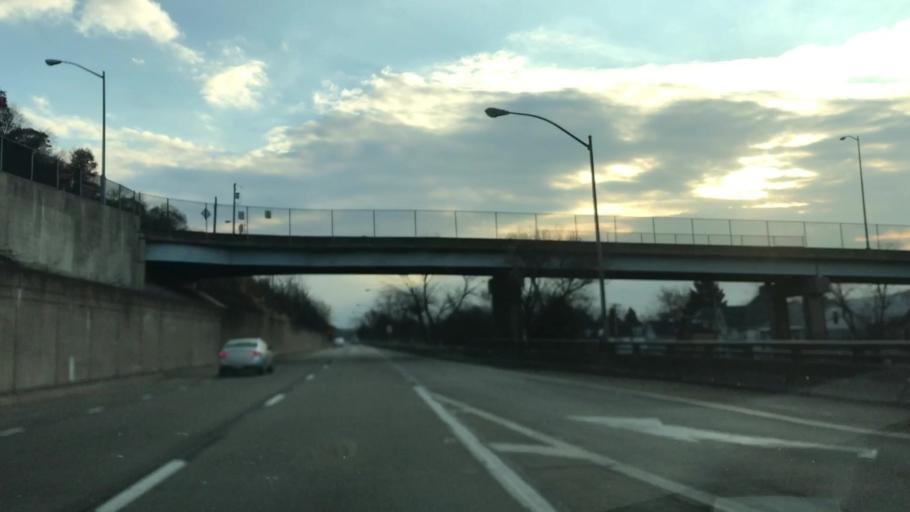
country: US
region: Pennsylvania
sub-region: Allegheny County
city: Emsworth
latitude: 40.5171
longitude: -80.1280
